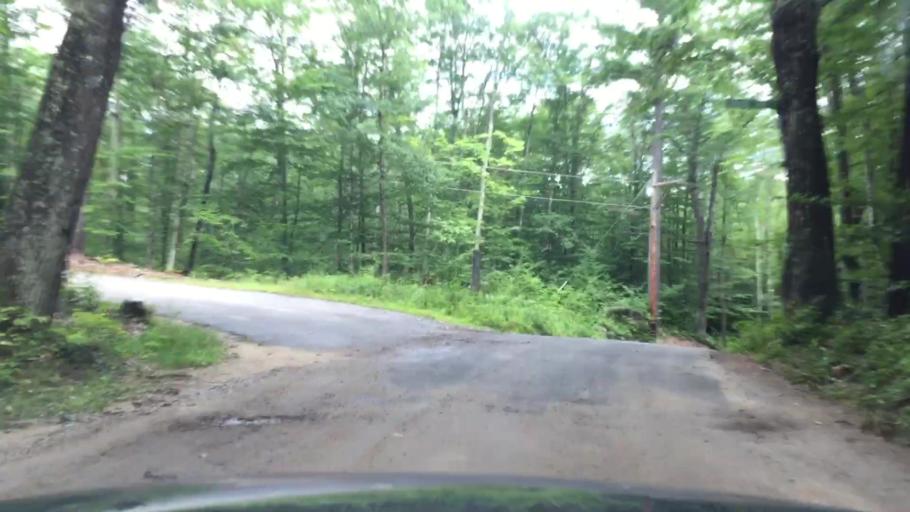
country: US
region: New Hampshire
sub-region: Carroll County
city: Sandwich
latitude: 43.7902
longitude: -71.4783
